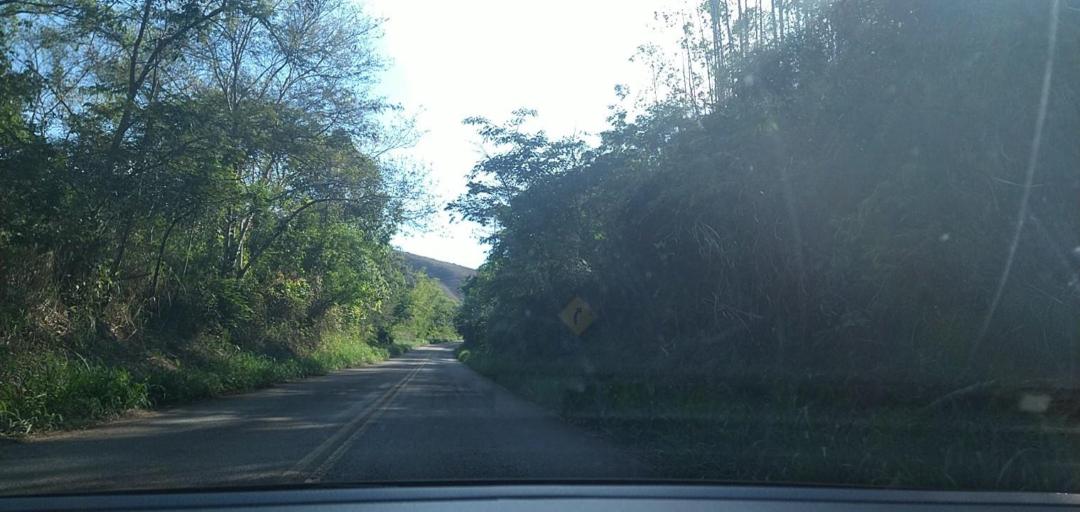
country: BR
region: Minas Gerais
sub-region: Alvinopolis
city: Alvinopolis
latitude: -20.1736
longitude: -42.9228
